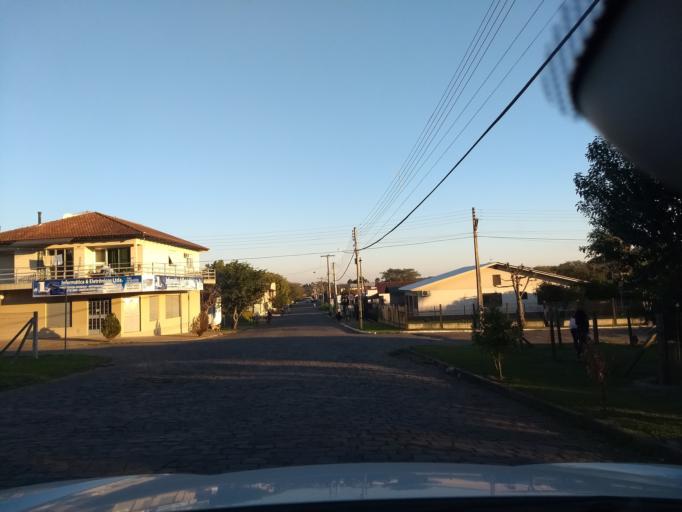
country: BR
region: Rio Grande do Sul
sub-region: Santa Cruz Do Sul
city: Santa Cruz do Sul
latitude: -29.7160
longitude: -52.5152
